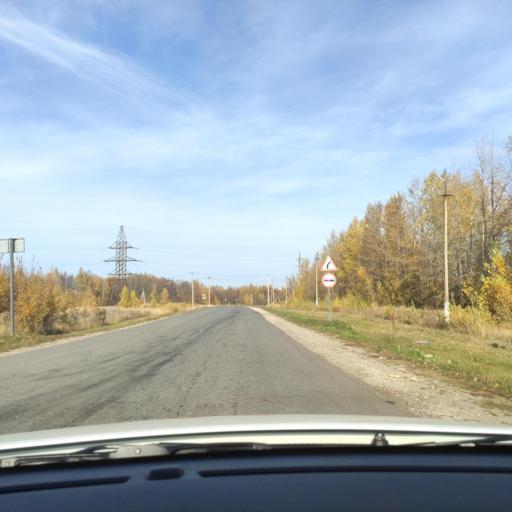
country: RU
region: Tatarstan
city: Pestretsy
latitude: 55.7236
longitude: 49.4563
